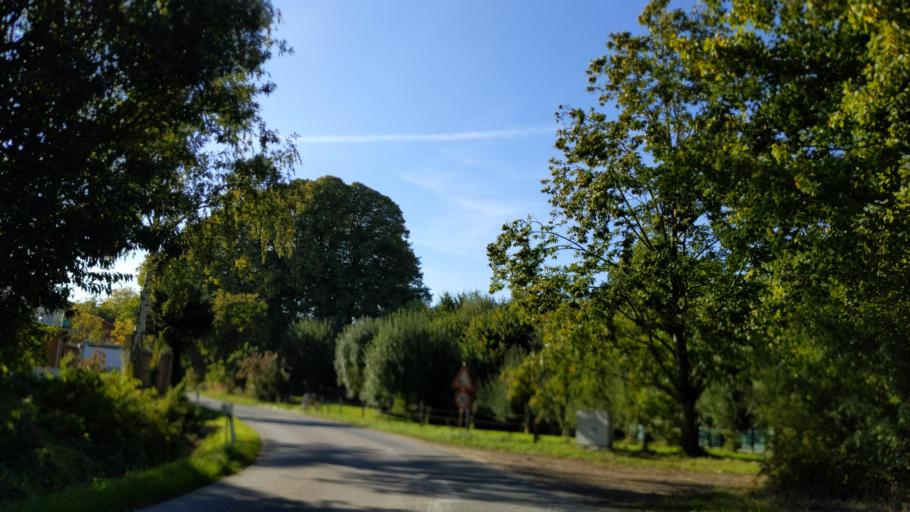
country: DE
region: Schleswig-Holstein
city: Ahrensbok
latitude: 53.9982
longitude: 10.6282
